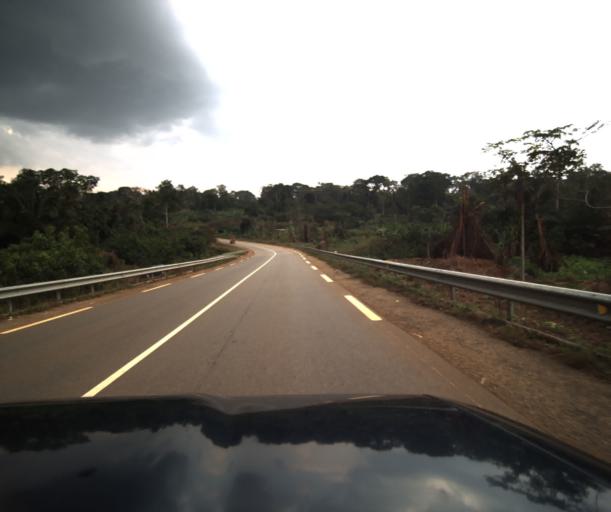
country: CM
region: Centre
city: Mbankomo
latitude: 3.6707
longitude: 11.3475
